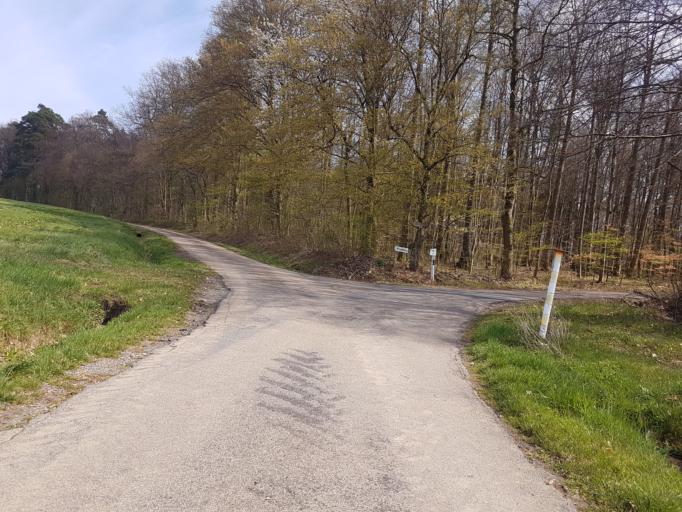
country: DE
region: Baden-Wuerttemberg
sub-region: Regierungsbezirk Stuttgart
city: Forchtenberg
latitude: 49.3675
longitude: 9.5557
